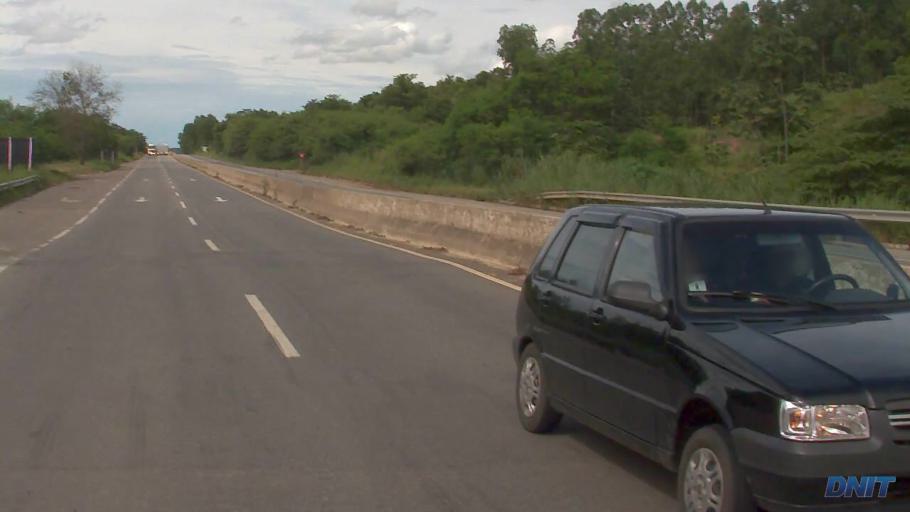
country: BR
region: Minas Gerais
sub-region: Ipaba
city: Ipaba
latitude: -19.3210
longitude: -42.4059
